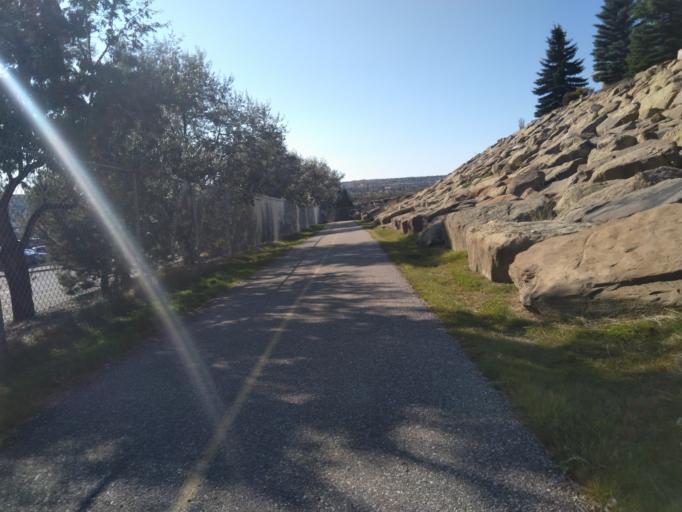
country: CA
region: Alberta
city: Calgary
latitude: 51.1476
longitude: -114.0853
